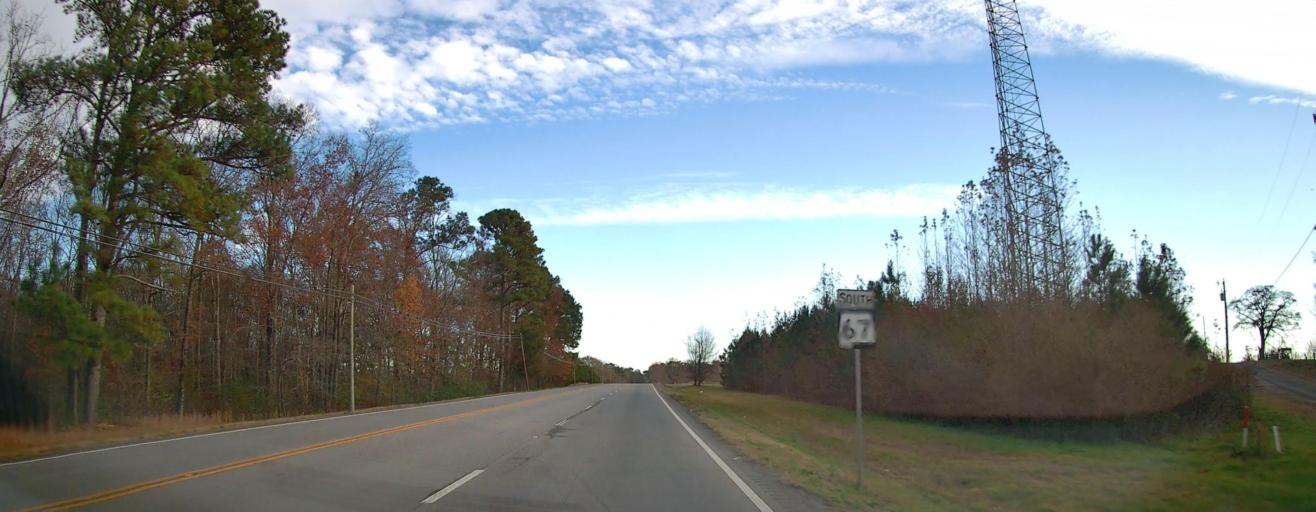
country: US
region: Alabama
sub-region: Marshall County
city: Arab
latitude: 34.3513
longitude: -86.6171
